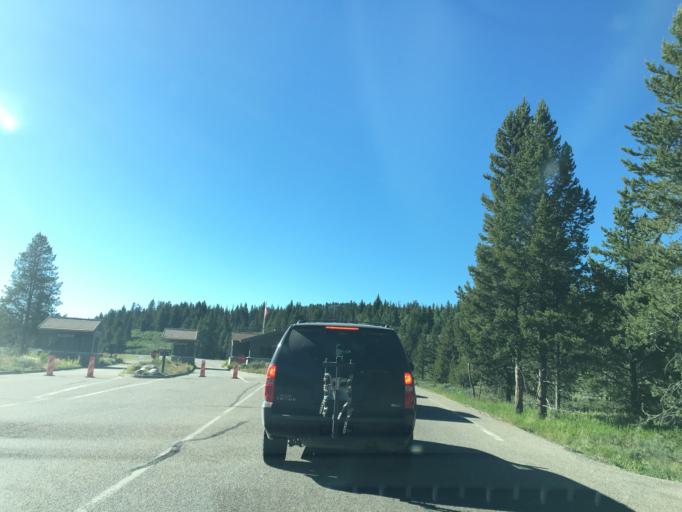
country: US
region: Wyoming
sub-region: Teton County
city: Jackson
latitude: 43.8435
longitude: -110.5117
